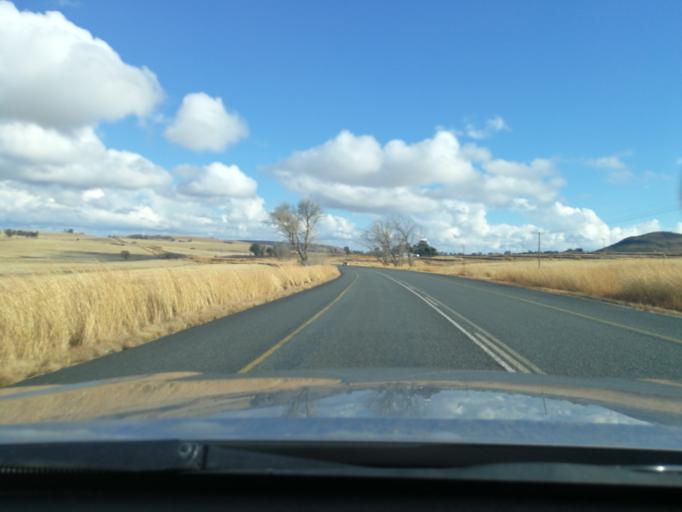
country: ZA
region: Orange Free State
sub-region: Thabo Mofutsanyana District Municipality
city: Reitz
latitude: -27.9748
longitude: 28.3743
